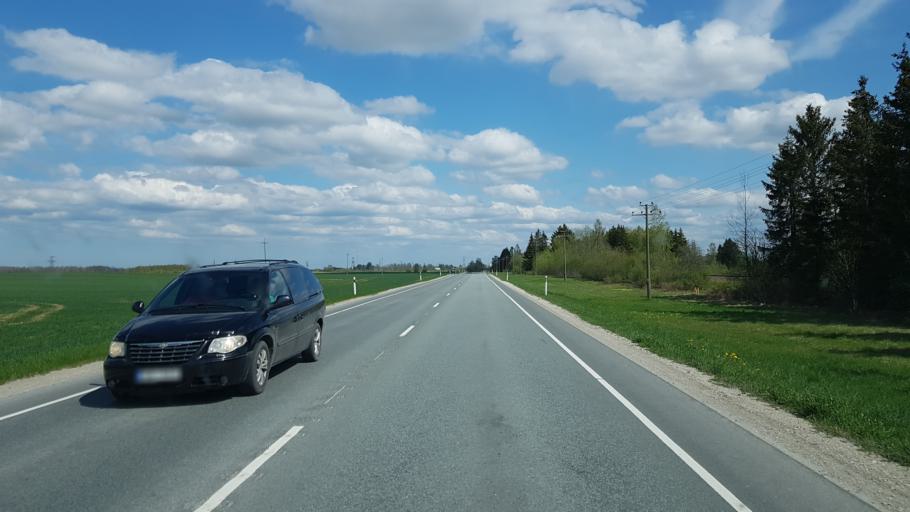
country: EE
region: Laeaene-Virumaa
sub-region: Rakvere linn
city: Rakvere
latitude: 59.3513
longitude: 26.3007
